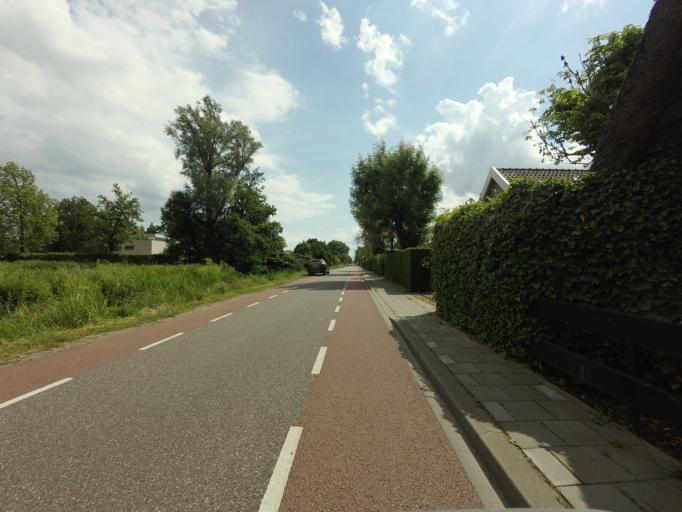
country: NL
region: North Holland
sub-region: Gemeente Wijdemeren
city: Oud-Loosdrecht
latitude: 52.1803
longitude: 5.0690
